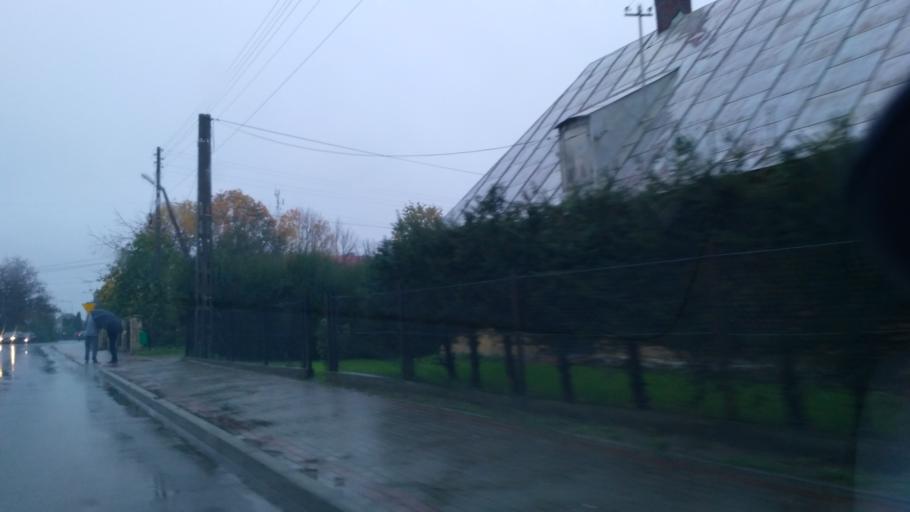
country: PL
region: Subcarpathian Voivodeship
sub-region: Powiat krosnienski
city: Miejsce Piastowe
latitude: 49.6473
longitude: 21.8108
